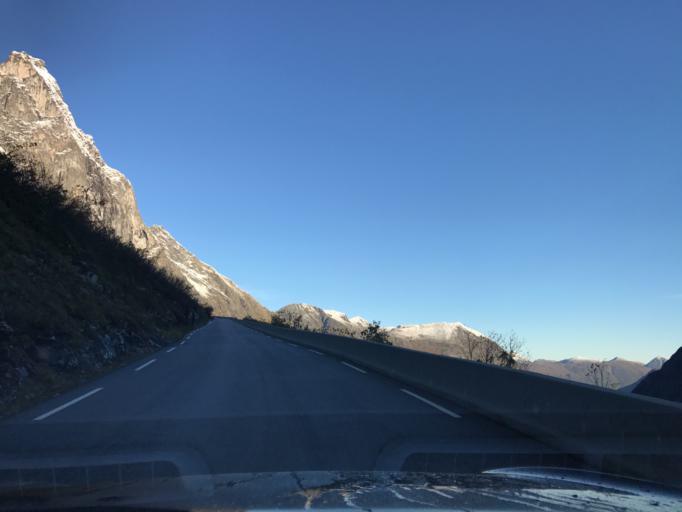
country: NO
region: More og Romsdal
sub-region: Rauma
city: Andalsnes
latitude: 62.4600
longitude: 7.6685
